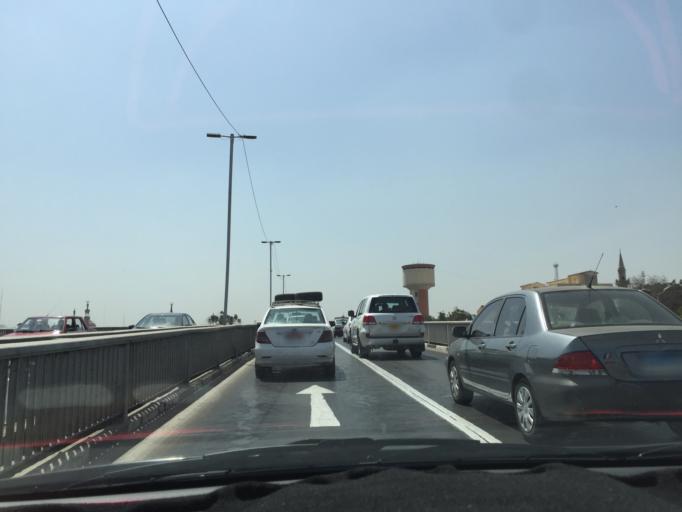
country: EG
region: Muhafazat al Qahirah
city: Cairo
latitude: 30.0563
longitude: 31.2805
